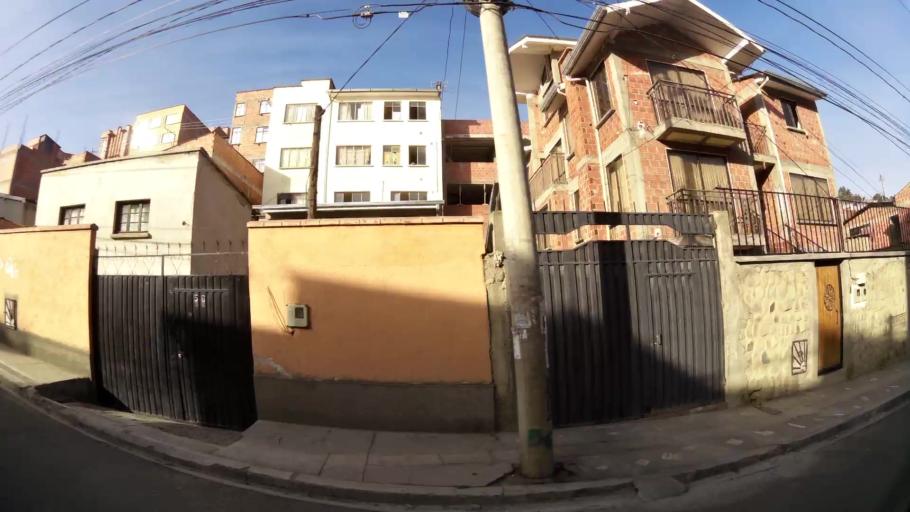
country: BO
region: La Paz
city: La Paz
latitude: -16.5284
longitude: -68.0952
